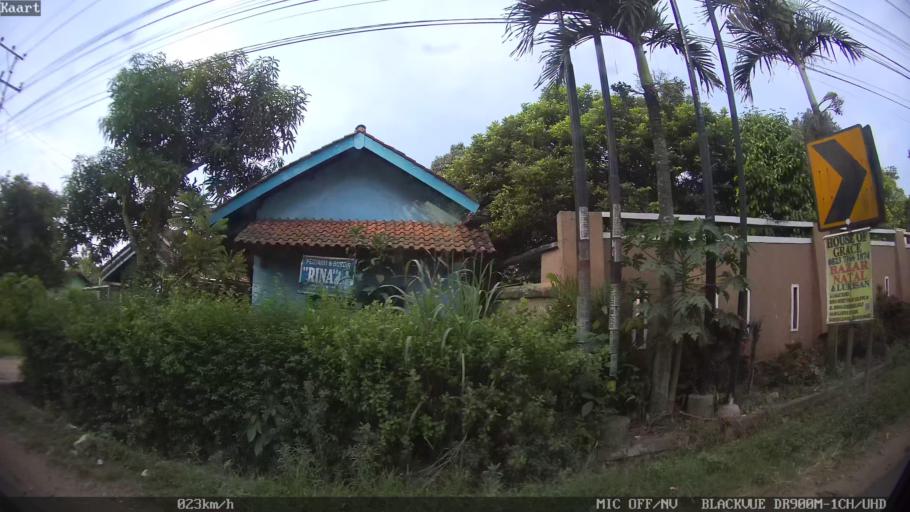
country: ID
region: Lampung
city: Natar
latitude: -5.3647
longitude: 105.1875
